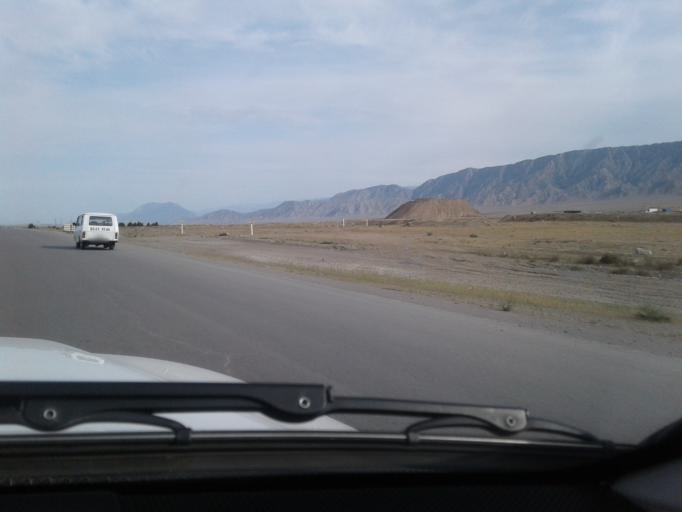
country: TM
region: Ahal
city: Arcabil
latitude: 38.2197
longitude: 57.8019
